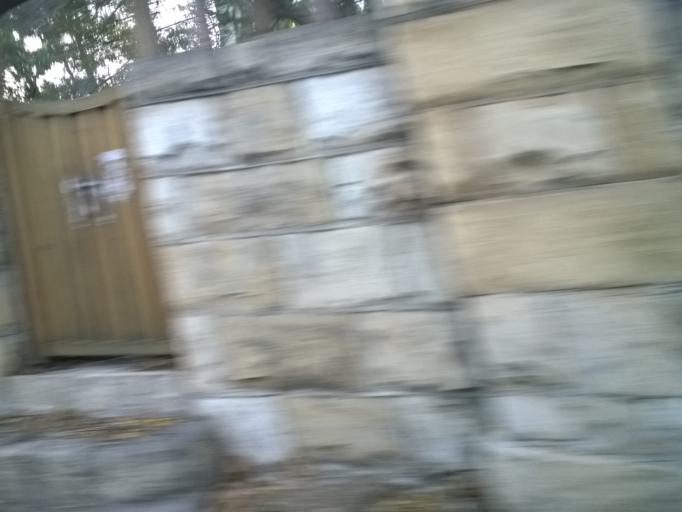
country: US
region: California
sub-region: Santa Barbara County
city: Mission Canyon
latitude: 34.4403
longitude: -119.7128
